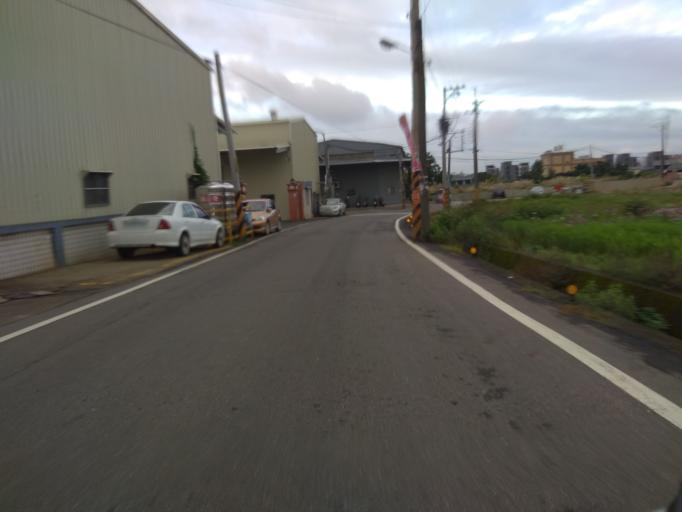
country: TW
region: Taiwan
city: Daxi
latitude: 24.9374
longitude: 121.1933
